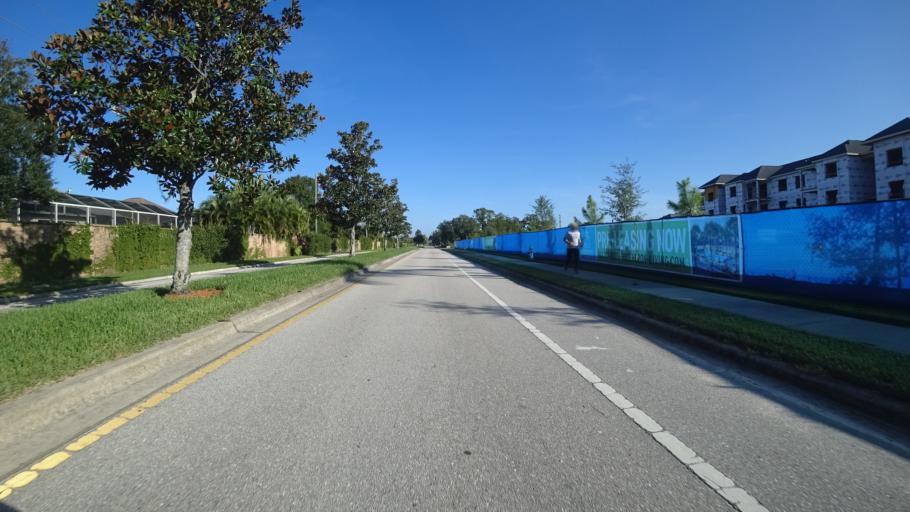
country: US
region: Florida
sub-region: Manatee County
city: Ellenton
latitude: 27.5023
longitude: -82.5019
